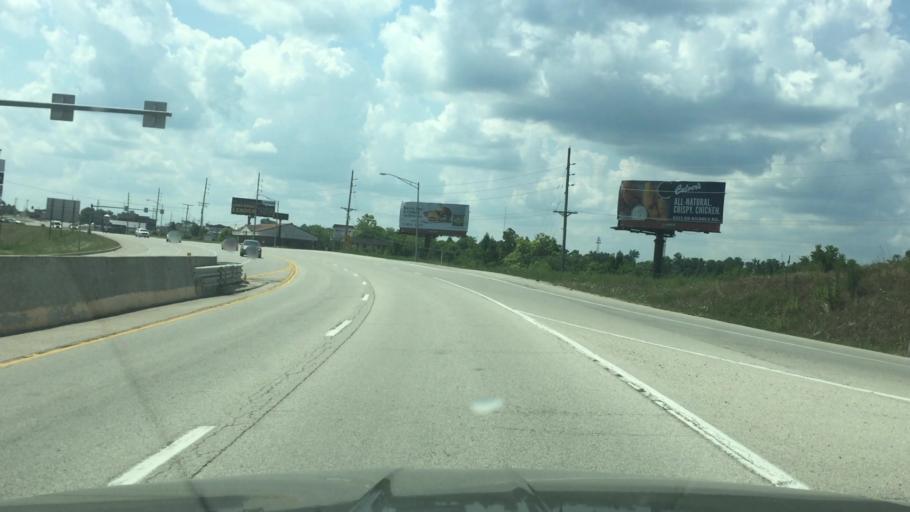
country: US
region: Missouri
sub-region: Miller County
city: Lake Ozark
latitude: 38.1749
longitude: -92.6153
